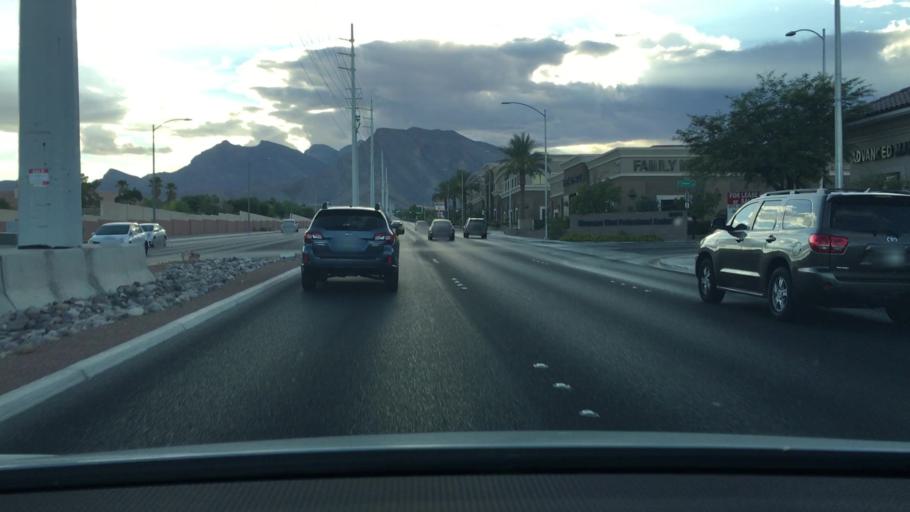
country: US
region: Nevada
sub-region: Clark County
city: Summerlin South
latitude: 36.2186
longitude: -115.2922
